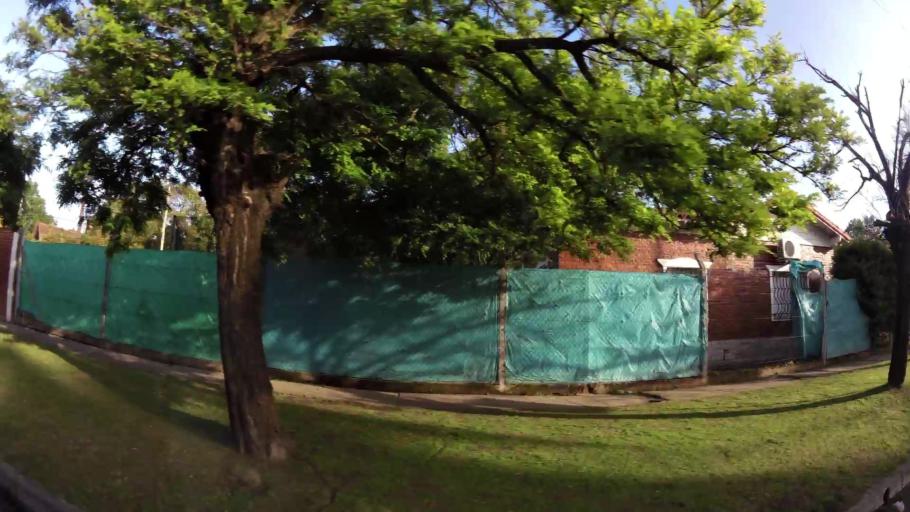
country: AR
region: Buenos Aires
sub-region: Partido de Quilmes
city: Quilmes
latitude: -34.7845
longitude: -58.2076
